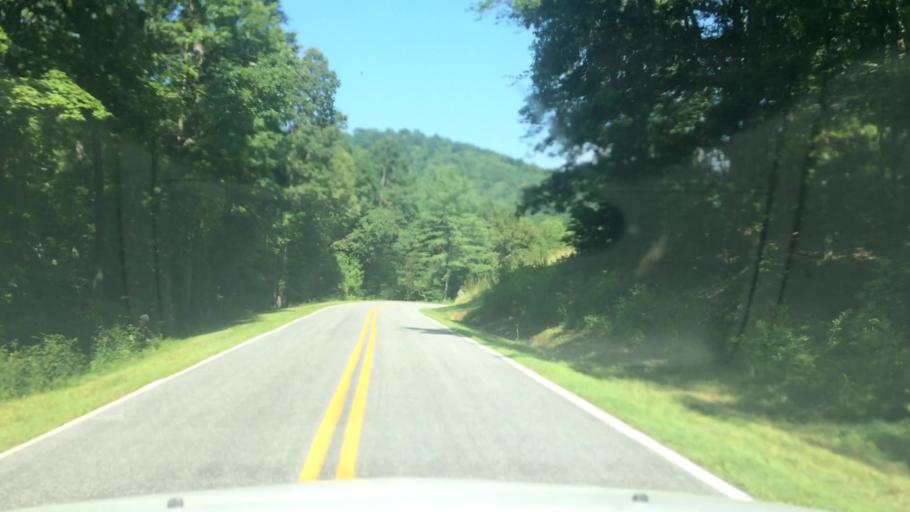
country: US
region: North Carolina
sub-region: Alexander County
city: Taylorsville
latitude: 35.9744
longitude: -81.2723
